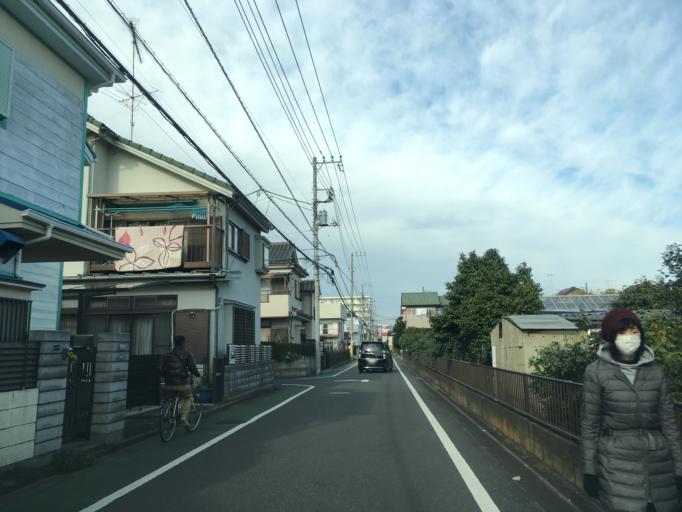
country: JP
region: Tokyo
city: Tanashicho
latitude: 35.7372
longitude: 139.5067
